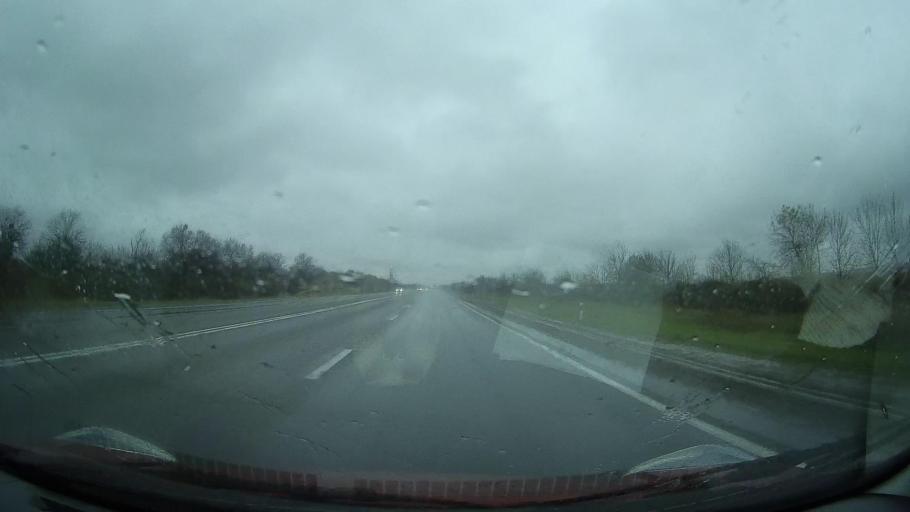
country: RU
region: Stavropol'skiy
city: Nevinnomyssk
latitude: 44.6328
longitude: 42.0156
